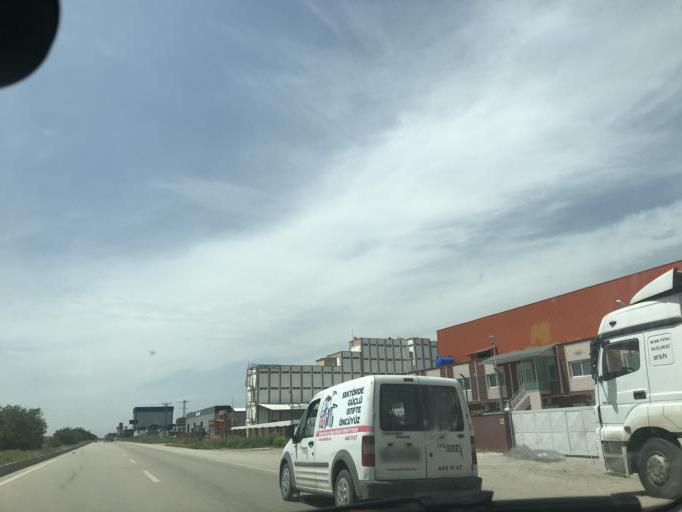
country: TR
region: Adana
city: Yakapinar
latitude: 36.9694
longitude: 35.5368
